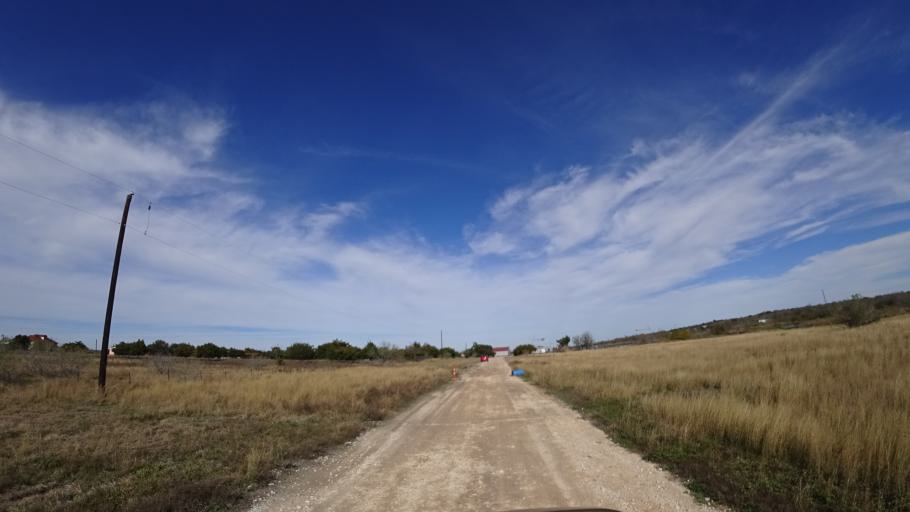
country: US
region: Texas
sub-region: Travis County
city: Onion Creek
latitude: 30.1115
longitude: -97.7164
